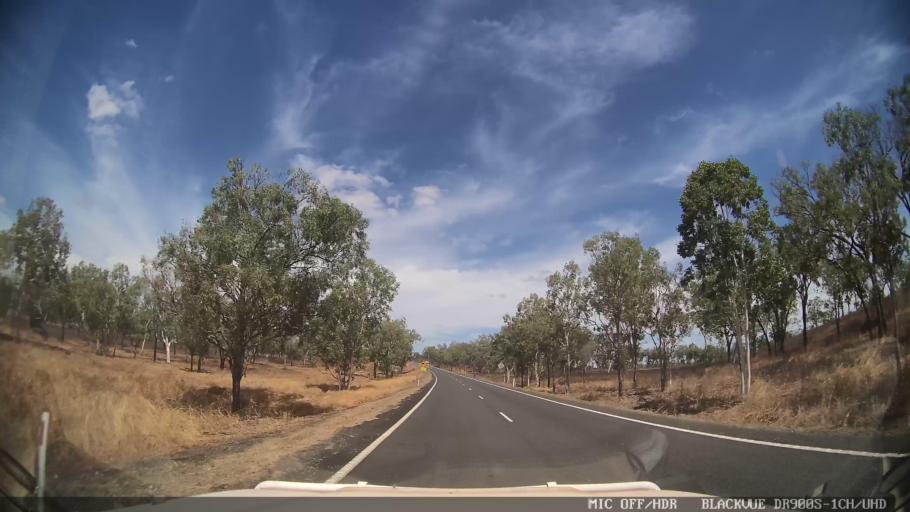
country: AU
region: Queensland
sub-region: Cook
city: Cooktown
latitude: -15.8001
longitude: 144.9235
